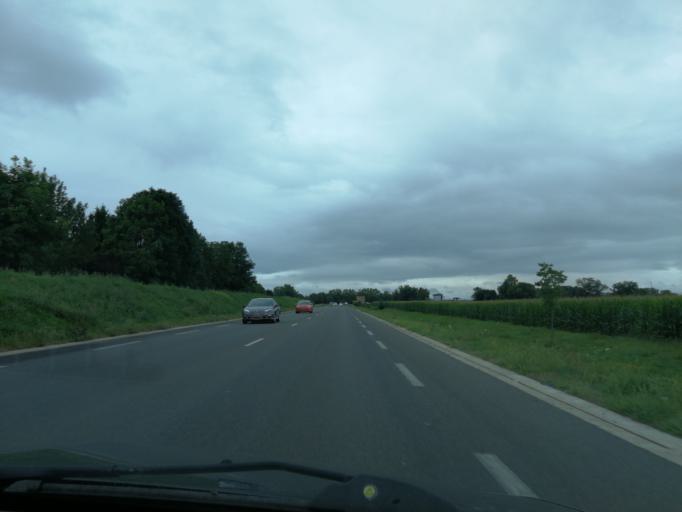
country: FR
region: Midi-Pyrenees
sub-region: Departement des Hautes-Pyrenees
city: Bazet
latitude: 43.2622
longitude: 0.0662
